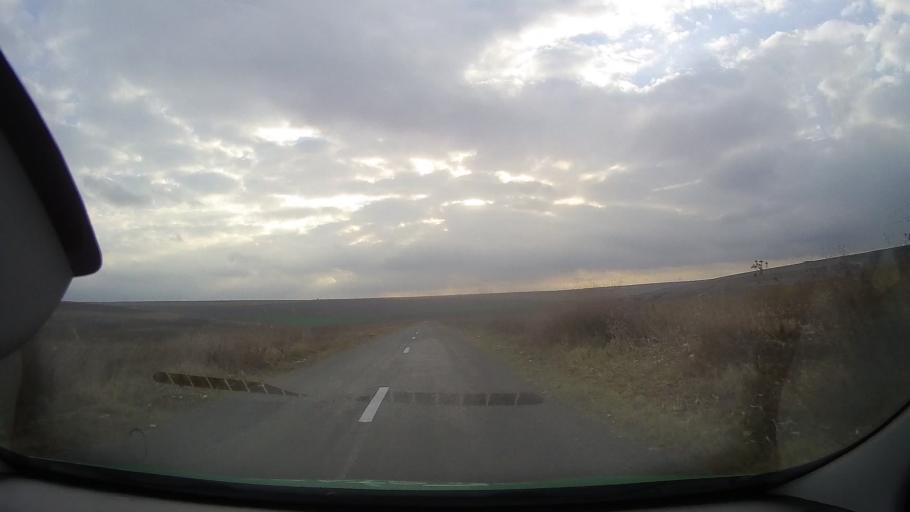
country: RO
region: Constanta
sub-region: Comuna Deleni
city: Pietreni
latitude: 44.1182
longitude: 28.1019
